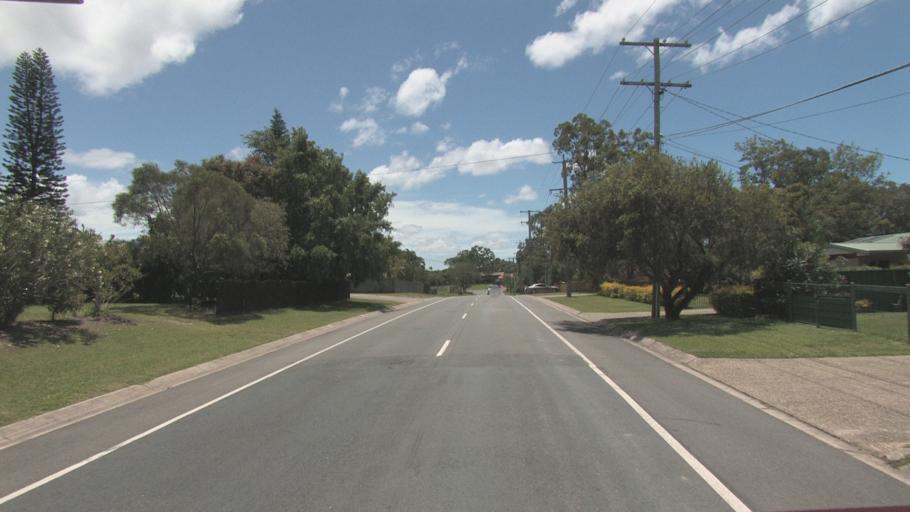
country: AU
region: Queensland
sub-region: Logan
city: Beenleigh
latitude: -27.6998
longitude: 153.2054
